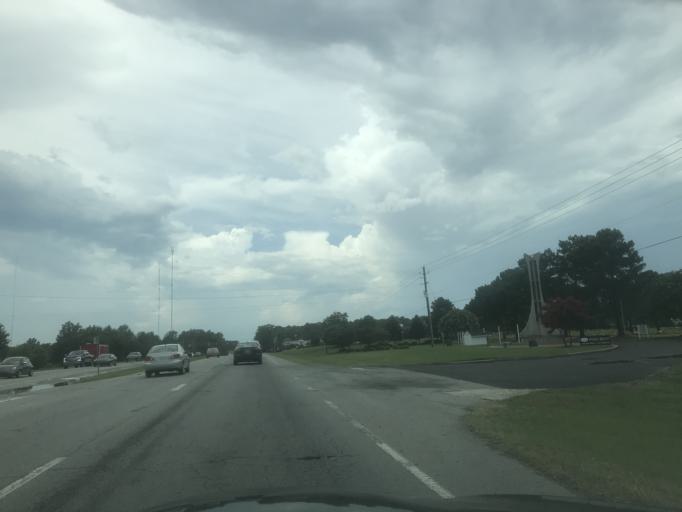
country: US
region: North Carolina
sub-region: Johnston County
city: Clayton
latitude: 35.6638
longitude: -78.4935
